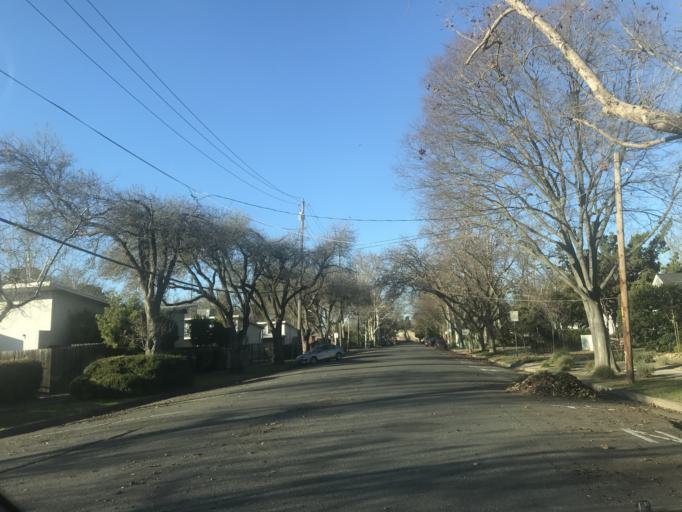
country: US
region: California
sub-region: Yolo County
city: Davis
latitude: 38.5470
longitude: -121.7445
